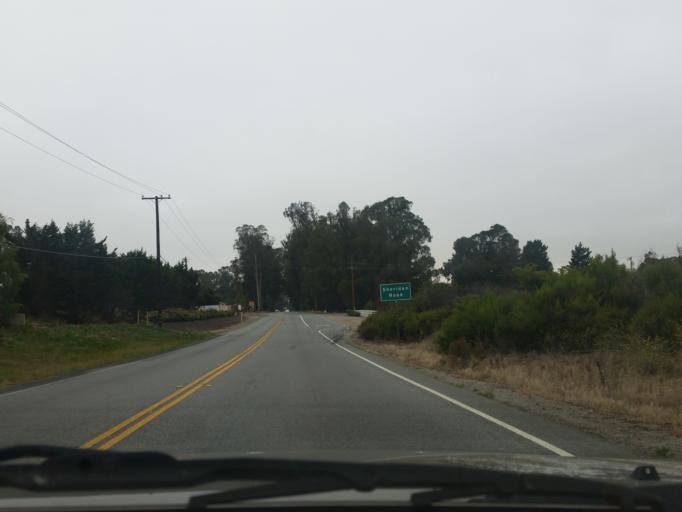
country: US
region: California
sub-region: San Luis Obispo County
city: Callender
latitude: 35.0473
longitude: -120.5750
